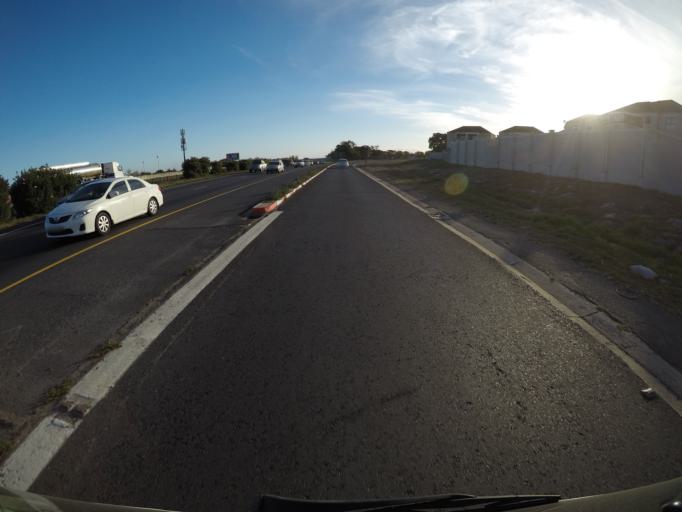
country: ZA
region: Western Cape
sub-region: City of Cape Town
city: Kraaifontein
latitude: -33.8634
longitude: 18.6867
